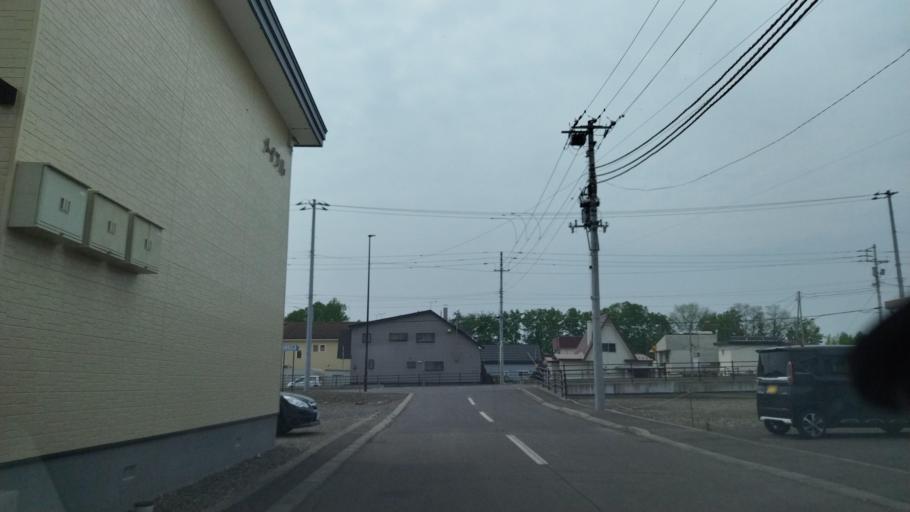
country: JP
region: Hokkaido
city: Obihiro
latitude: 42.9121
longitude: 143.0597
